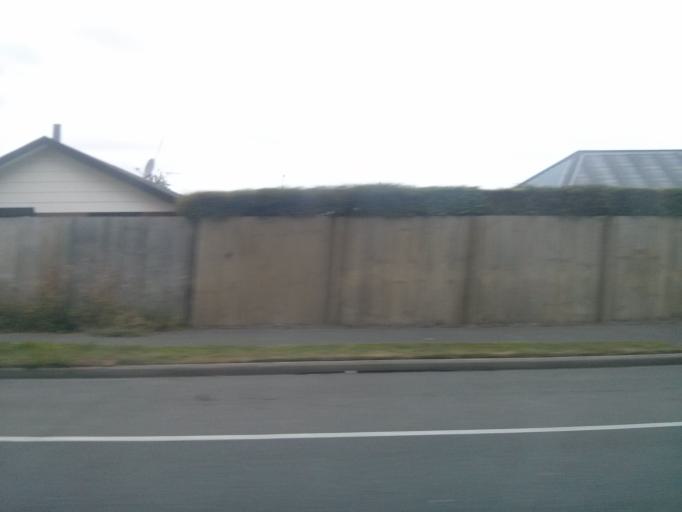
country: NZ
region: Canterbury
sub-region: Christchurch City
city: Christchurch
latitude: -43.4565
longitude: 172.6250
